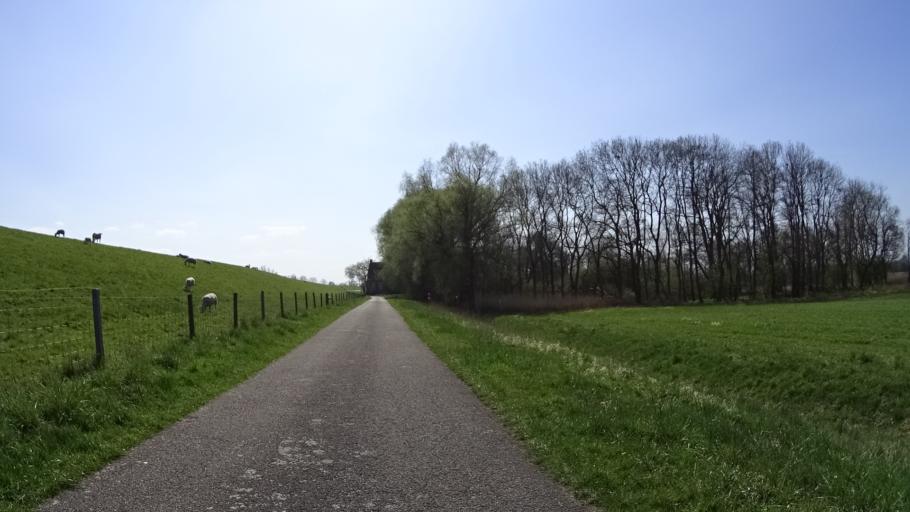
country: DE
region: Lower Saxony
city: Weener
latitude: 53.1186
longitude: 7.3716
